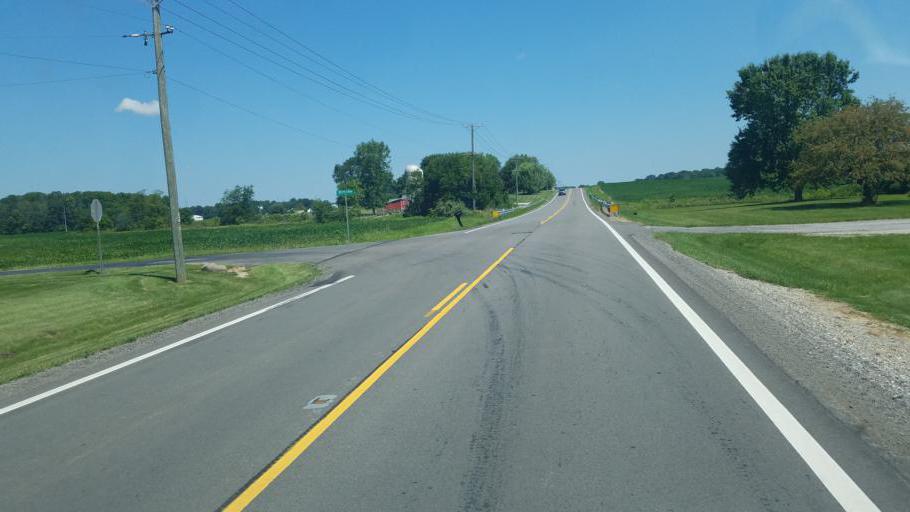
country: US
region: Ohio
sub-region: Marion County
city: Marion
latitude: 40.4840
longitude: -83.0689
